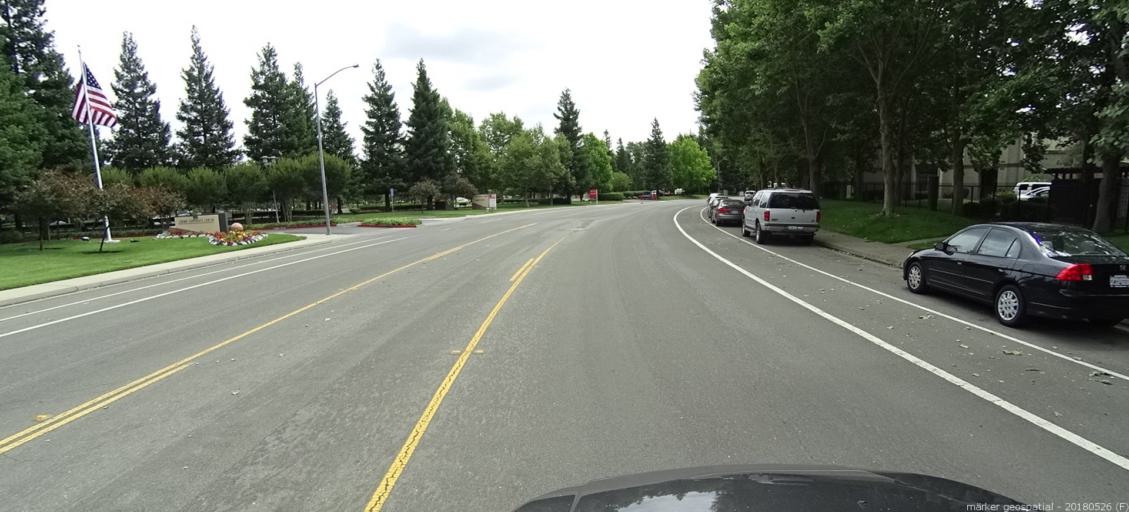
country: US
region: California
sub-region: Yolo County
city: West Sacramento
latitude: 38.6203
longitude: -121.5201
